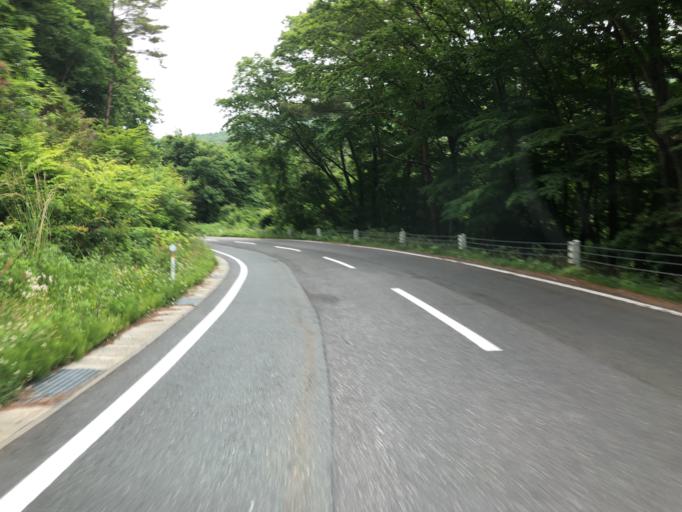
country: JP
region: Fukushima
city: Funehikimachi-funehiki
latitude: 37.3820
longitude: 140.7173
